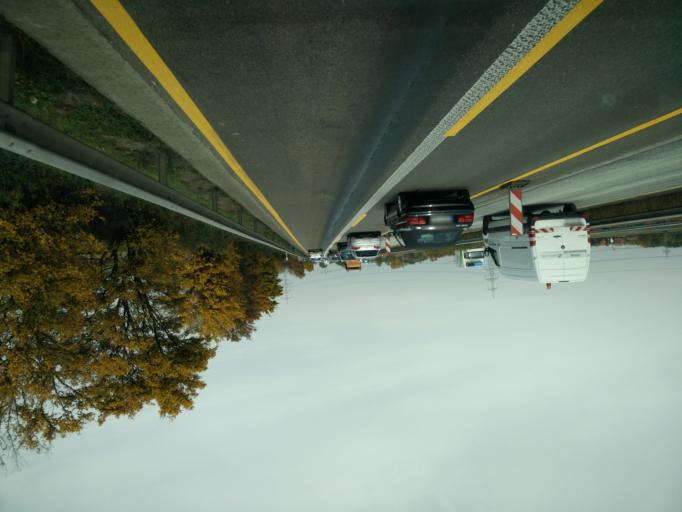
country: DE
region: Rheinland-Pfalz
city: Hessheim
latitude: 49.5322
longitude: 8.3147
